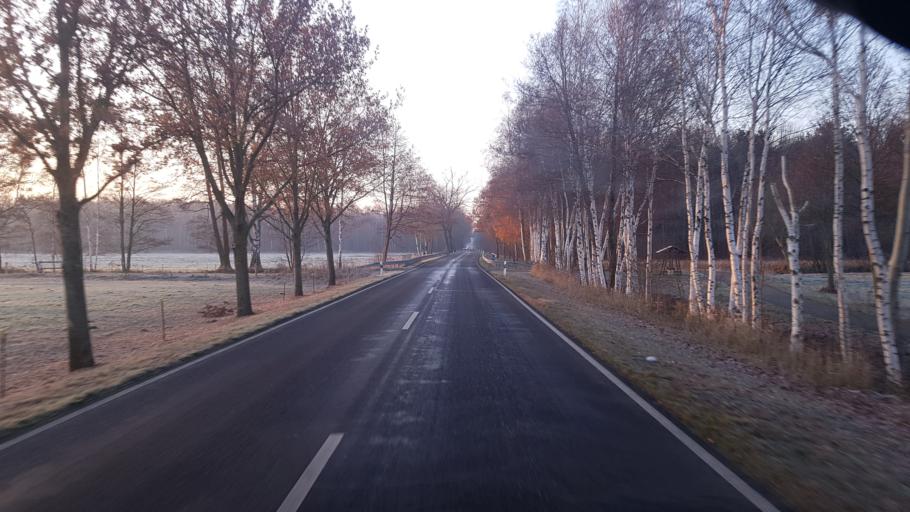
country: DE
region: Brandenburg
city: Tettau
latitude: 51.4494
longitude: 13.7370
